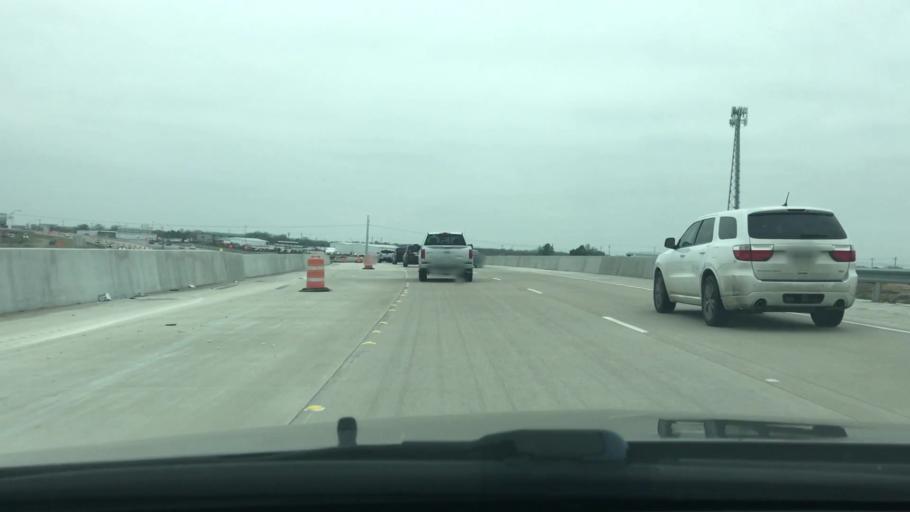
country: US
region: Texas
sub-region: Navarro County
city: Corsicana
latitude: 32.0663
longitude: -96.4518
